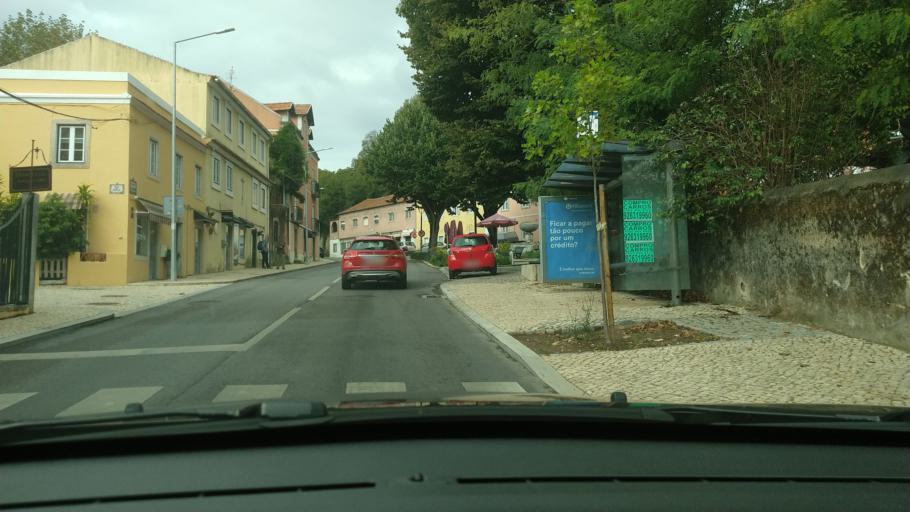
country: PT
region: Lisbon
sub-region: Sintra
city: Sintra
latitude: 38.7902
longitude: -9.3771
